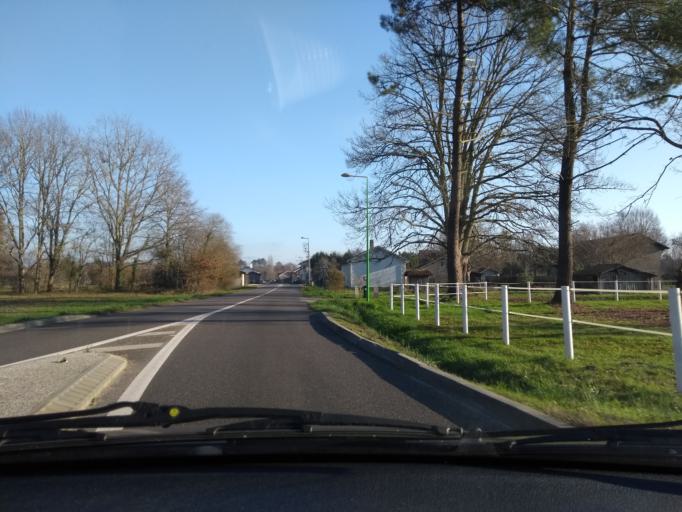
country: FR
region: Aquitaine
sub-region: Departement de la Gironde
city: Mios
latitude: 44.5923
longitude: -0.8998
